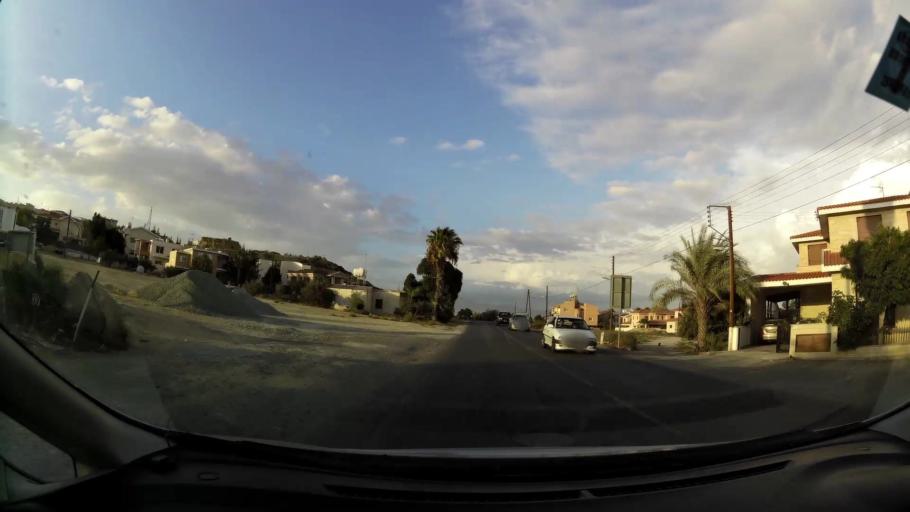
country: CY
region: Lefkosia
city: Nicosia
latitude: 35.1597
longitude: 33.3980
